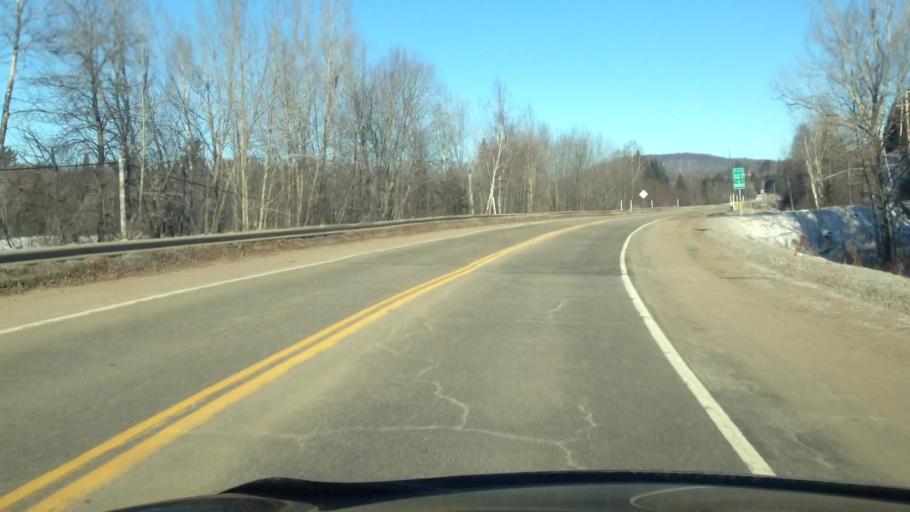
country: CA
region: Quebec
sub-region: Laurentides
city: Mont-Tremblant
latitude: 46.0730
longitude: -74.6218
